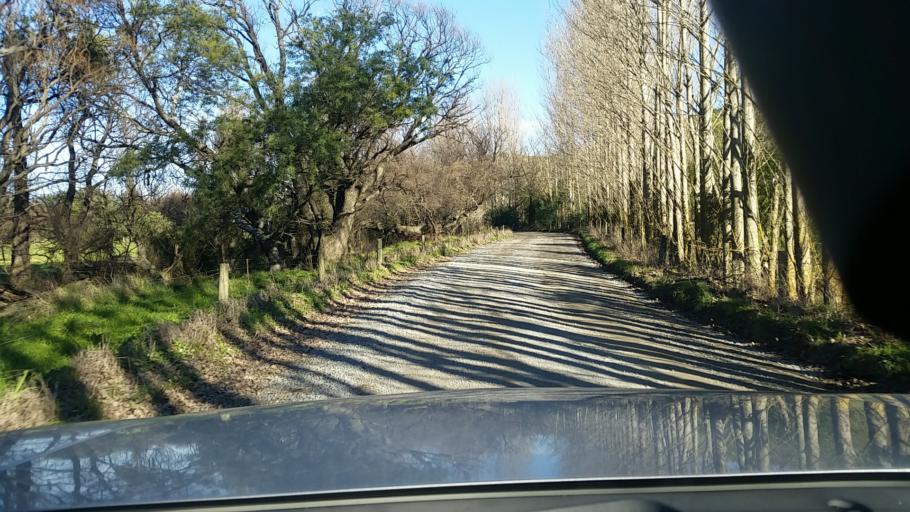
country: NZ
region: Marlborough
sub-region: Marlborough District
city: Blenheim
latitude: -41.4422
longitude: 173.8982
